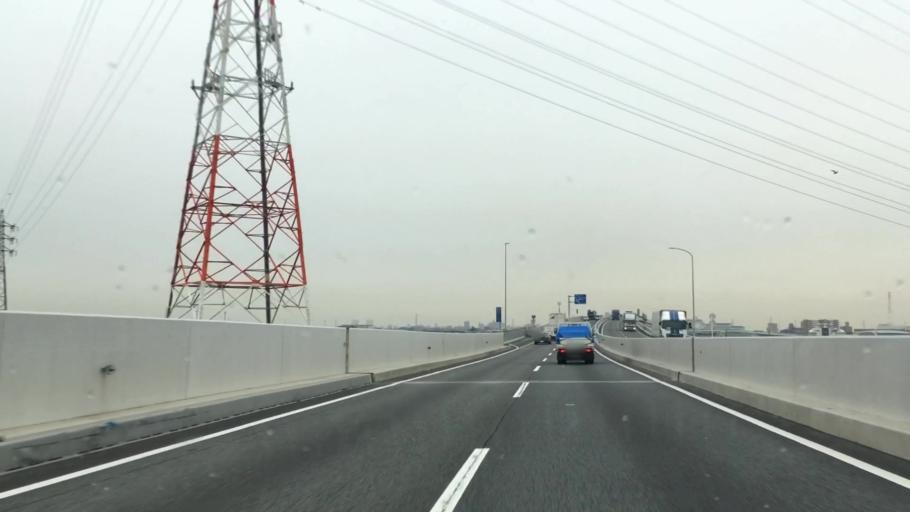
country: JP
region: Aichi
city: Chiryu
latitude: 34.9948
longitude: 137.0338
